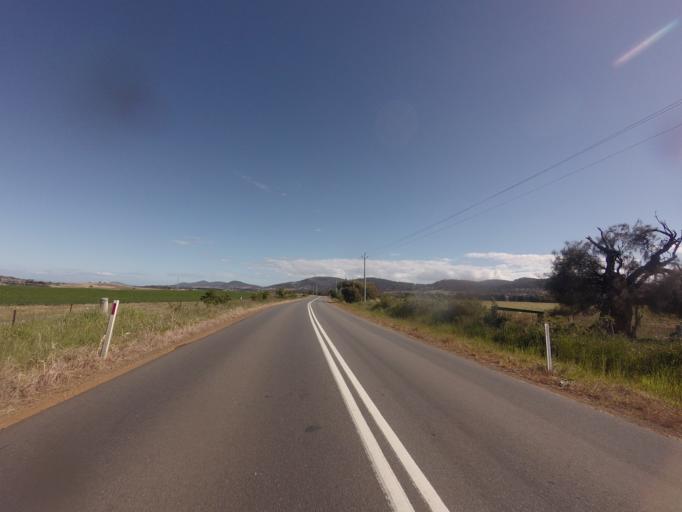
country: AU
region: Tasmania
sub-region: Clarence
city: Cambridge
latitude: -42.7583
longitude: 147.4163
